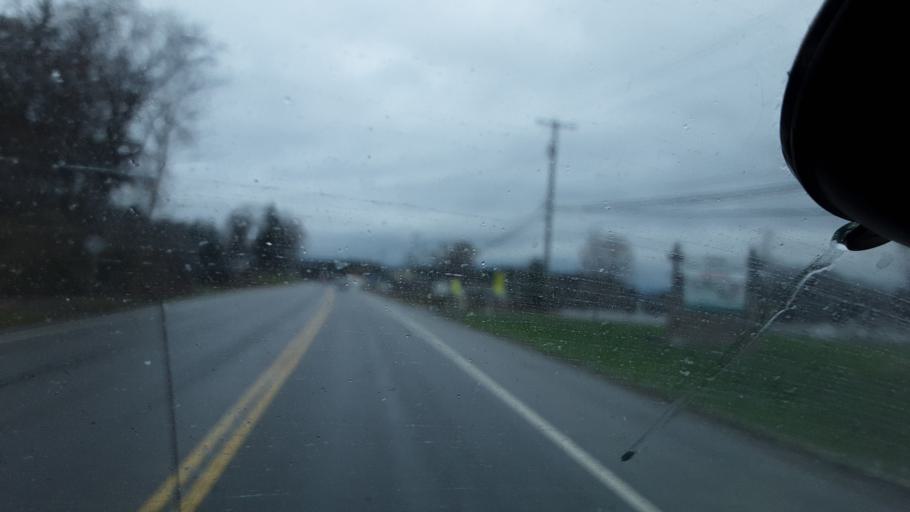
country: US
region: New York
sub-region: Cattaraugus County
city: Yorkshire
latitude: 42.5864
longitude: -78.4918
